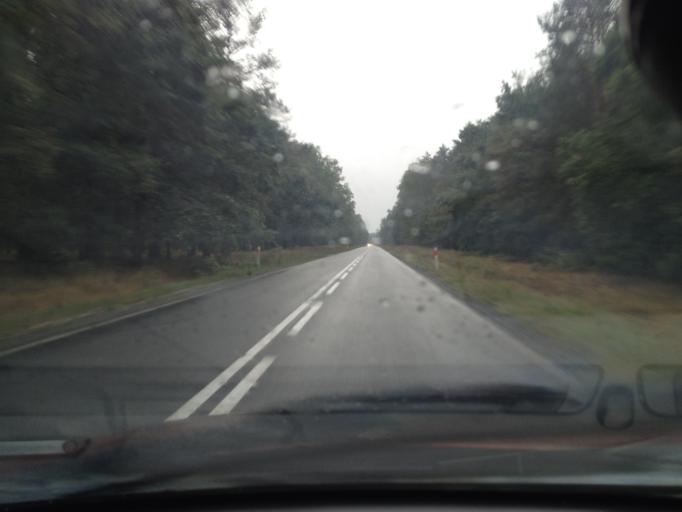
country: PL
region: Lubusz
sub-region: Powiat zaganski
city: Ilowa
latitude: 51.5499
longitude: 15.2551
